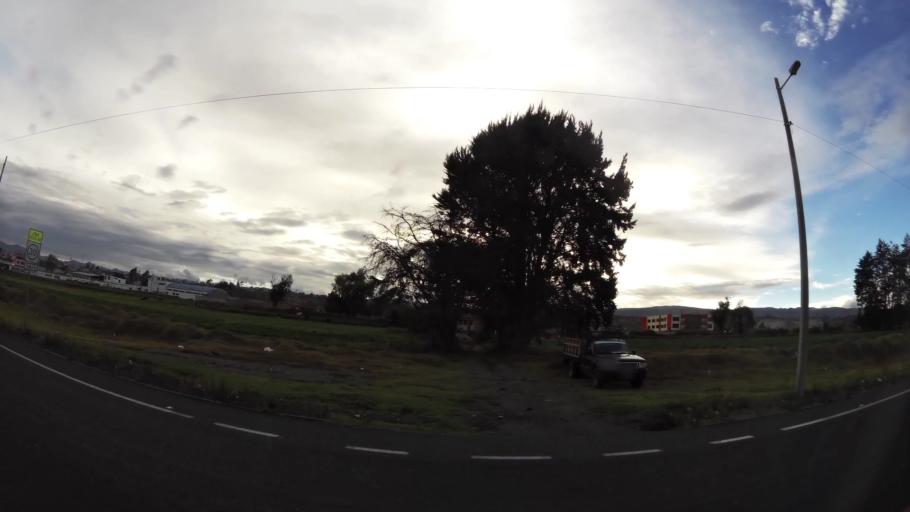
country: EC
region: Cotopaxi
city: Latacunga
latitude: -0.9215
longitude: -78.6264
